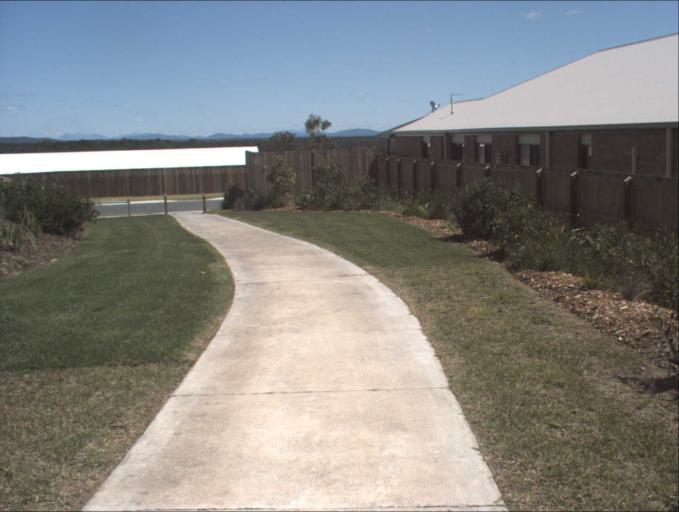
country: AU
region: Queensland
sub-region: Logan
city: Waterford West
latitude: -27.7166
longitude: 153.1565
